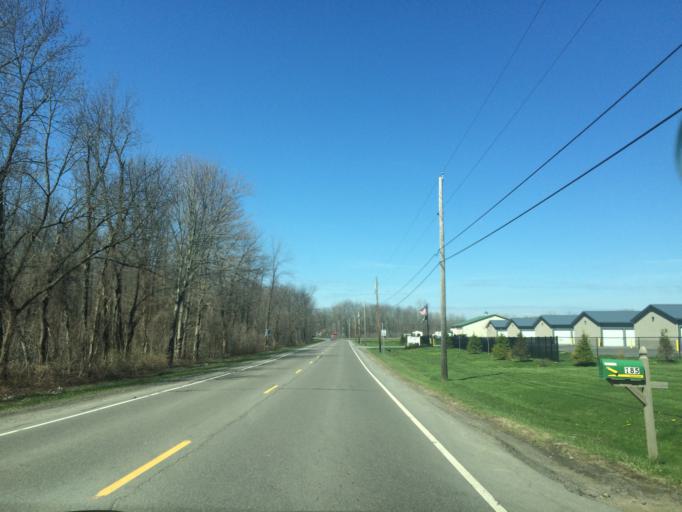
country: US
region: New York
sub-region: Monroe County
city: Fairport
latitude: 43.0960
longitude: -77.3680
